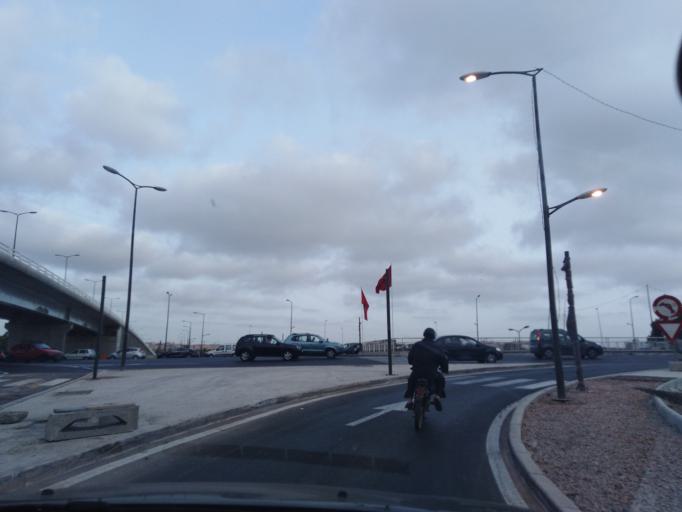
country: MA
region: Grand Casablanca
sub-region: Casablanca
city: Casablanca
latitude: 33.5387
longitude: -7.6627
